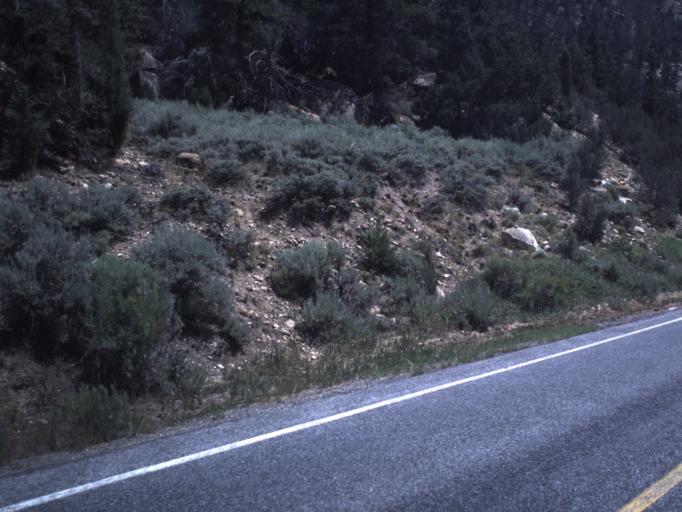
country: US
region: Utah
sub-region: Emery County
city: Huntington
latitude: 39.4359
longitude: -111.1322
